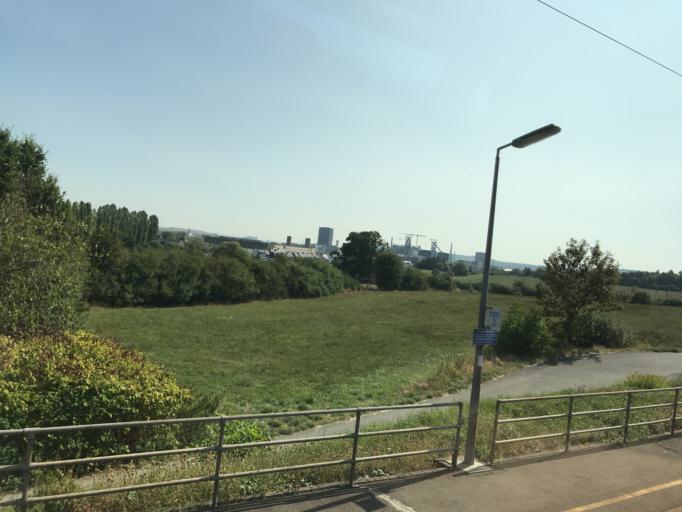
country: LU
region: Luxembourg
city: Belvaux
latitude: 49.5029
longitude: 5.9241
